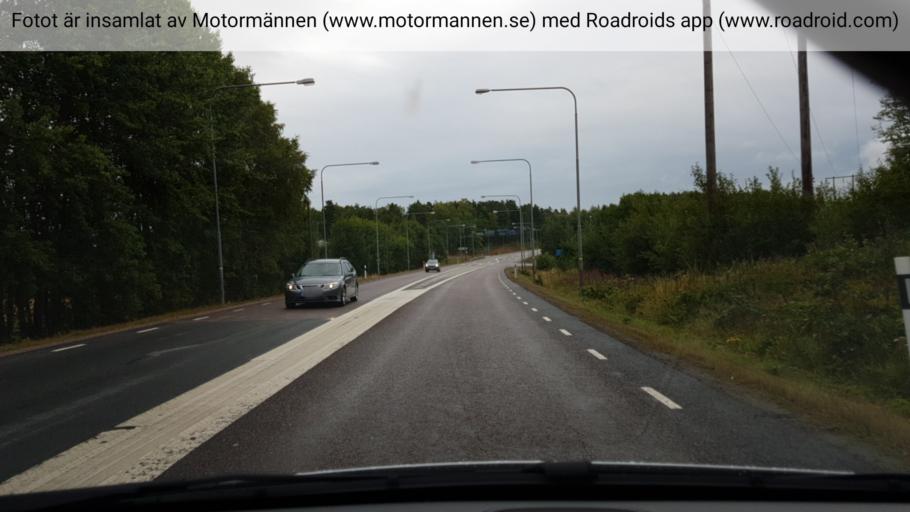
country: SE
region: Vaestra Goetaland
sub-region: Karlsborgs Kommun
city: Molltorp
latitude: 58.4892
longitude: 14.4100
